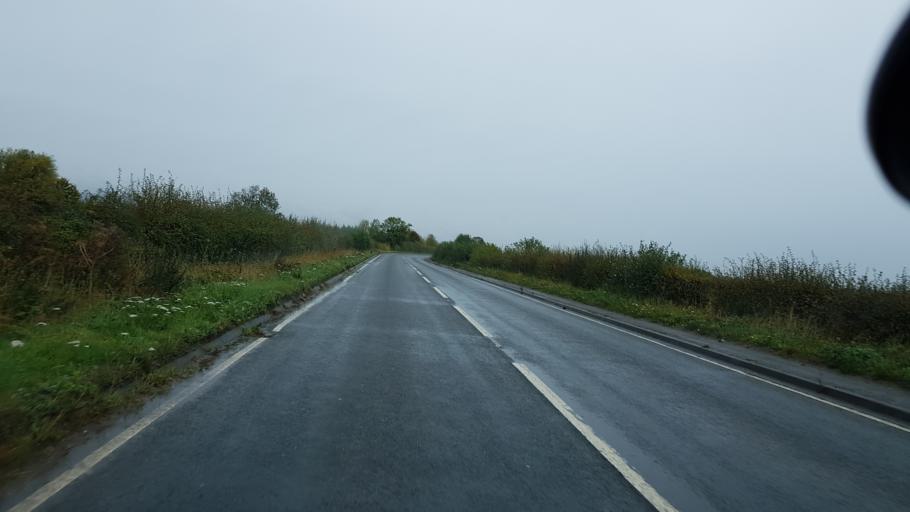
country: GB
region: England
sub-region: Worcestershire
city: Upton upon Severn
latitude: 52.0548
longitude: -2.1896
